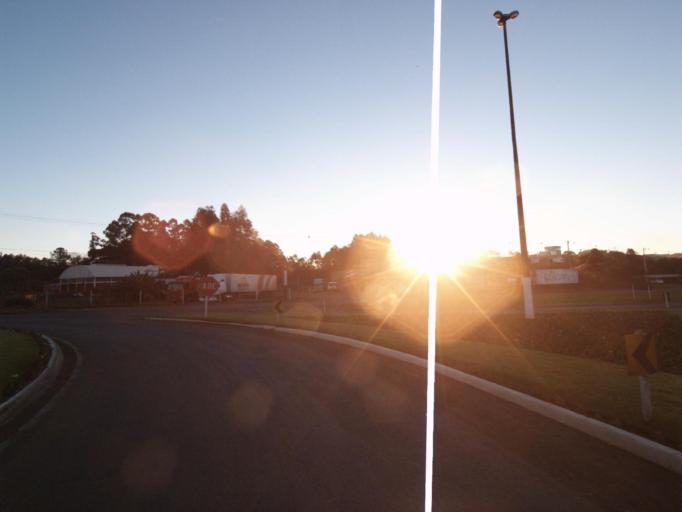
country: BR
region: Santa Catarina
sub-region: Sao Lourenco Do Oeste
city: Sao Lourenco dOeste
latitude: -26.7821
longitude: -53.1971
